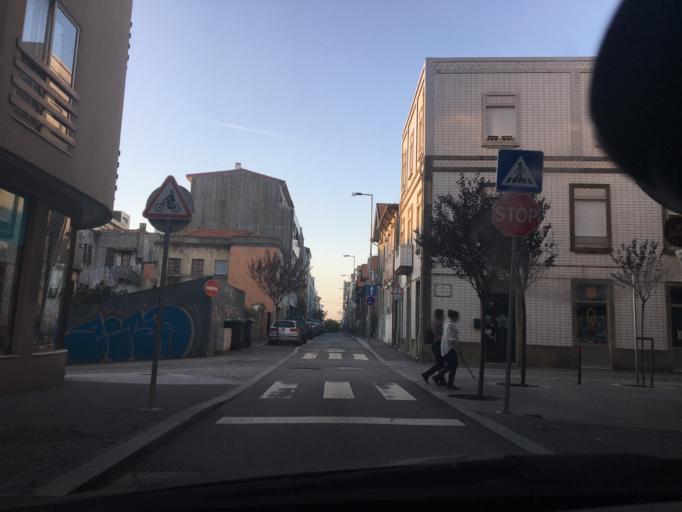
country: PT
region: Porto
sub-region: Matosinhos
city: Matosinhos
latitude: 41.1844
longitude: -8.6914
